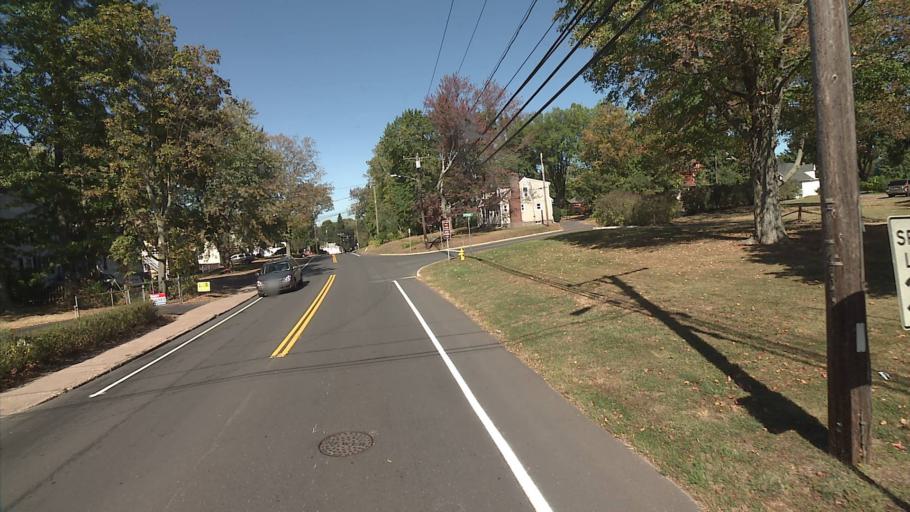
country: US
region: Connecticut
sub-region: Hartford County
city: Manchester
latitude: 41.7573
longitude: -72.5207
